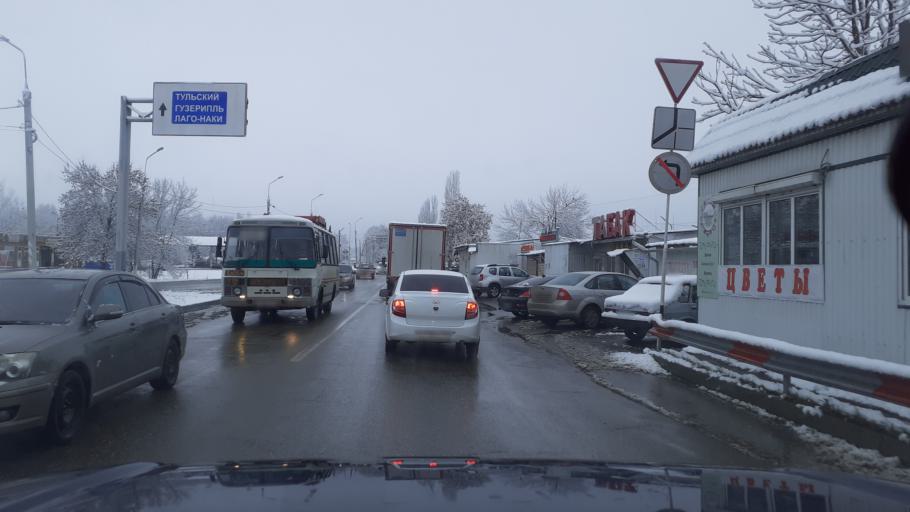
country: RU
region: Adygeya
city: Maykop
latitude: 44.5745
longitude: 40.1335
